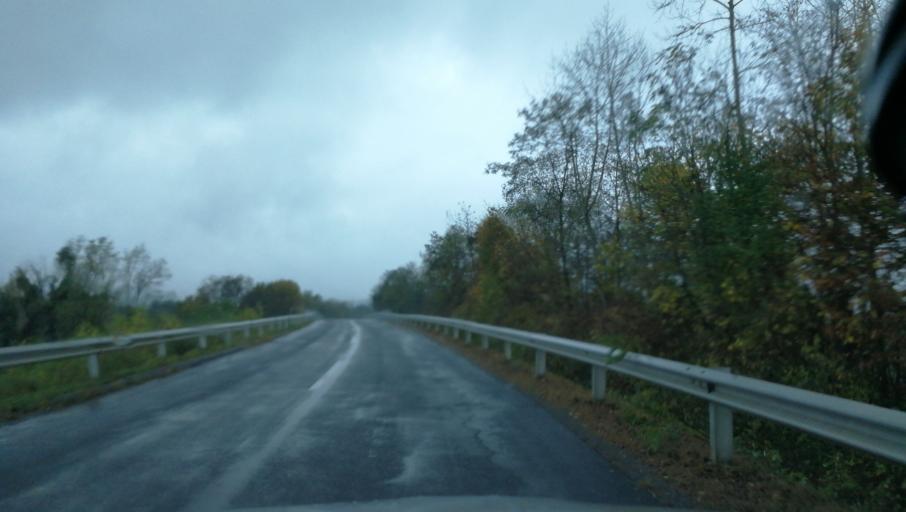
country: AT
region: Styria
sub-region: Politischer Bezirk Leibnitz
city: Sankt Veit am Vogau
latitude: 46.7417
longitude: 15.6178
